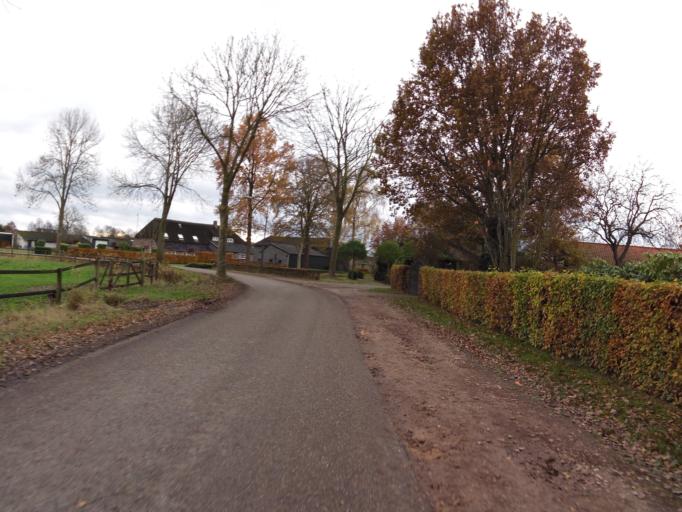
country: NL
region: North Brabant
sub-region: Gemeente Sint-Michielsgestel
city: Sint-Michielsgestel
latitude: 51.6648
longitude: 5.3916
